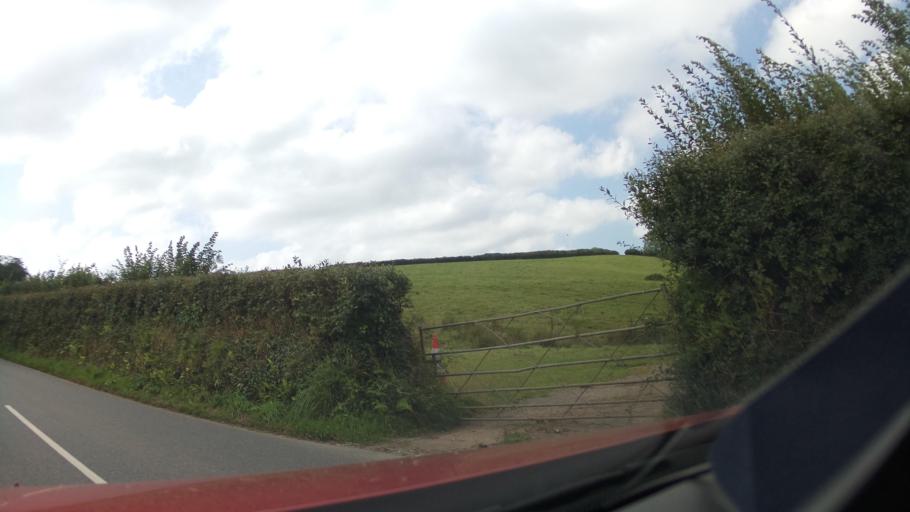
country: GB
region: England
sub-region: Devon
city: South Brent
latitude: 50.4050
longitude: -3.8226
